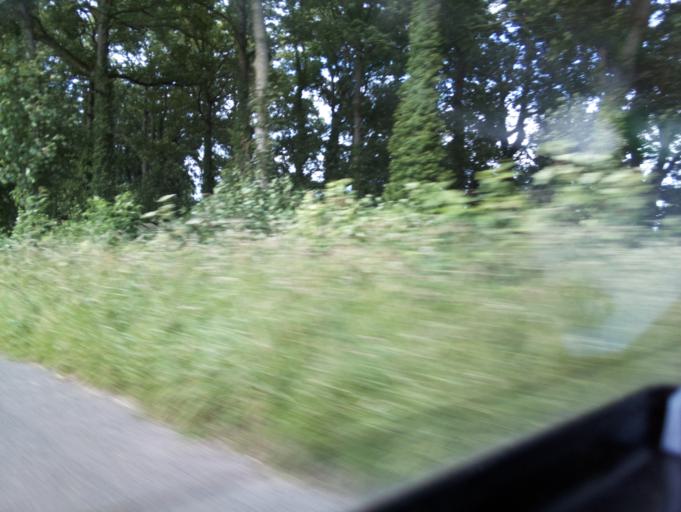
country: GB
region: England
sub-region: Gloucestershire
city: Donnington
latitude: 51.9774
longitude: -1.7550
